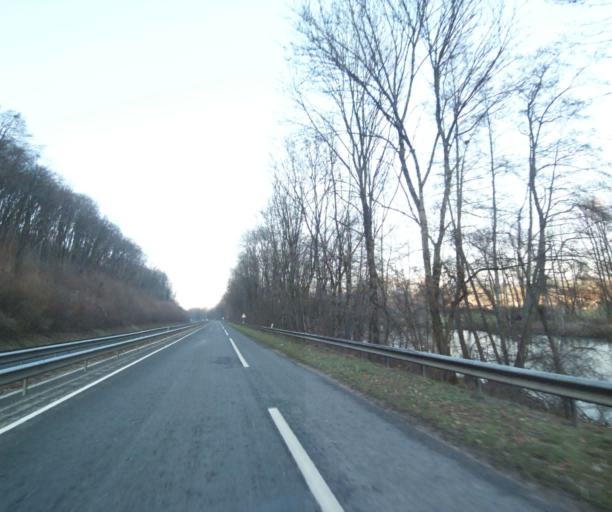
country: FR
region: Champagne-Ardenne
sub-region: Departement de la Haute-Marne
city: Chevillon
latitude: 48.5355
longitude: 5.0981
